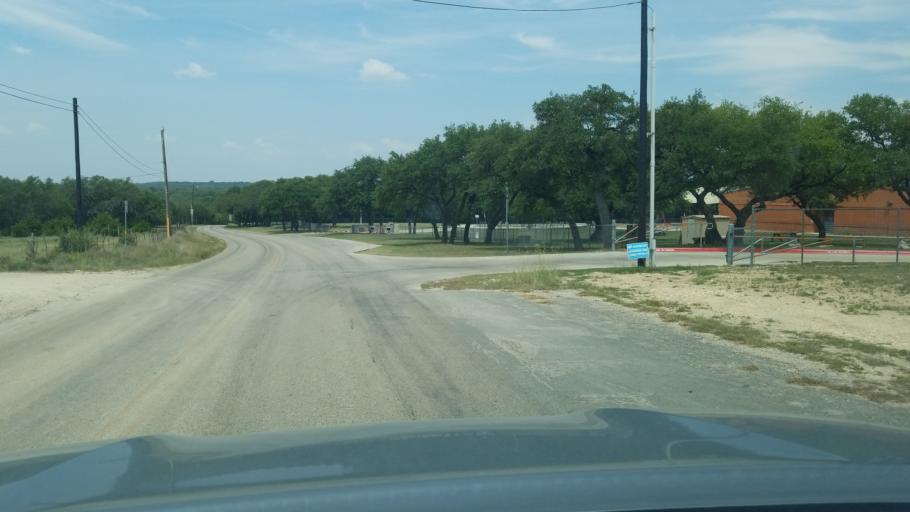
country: US
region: Texas
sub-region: Comal County
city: Bulverde
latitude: 29.7599
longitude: -98.4610
